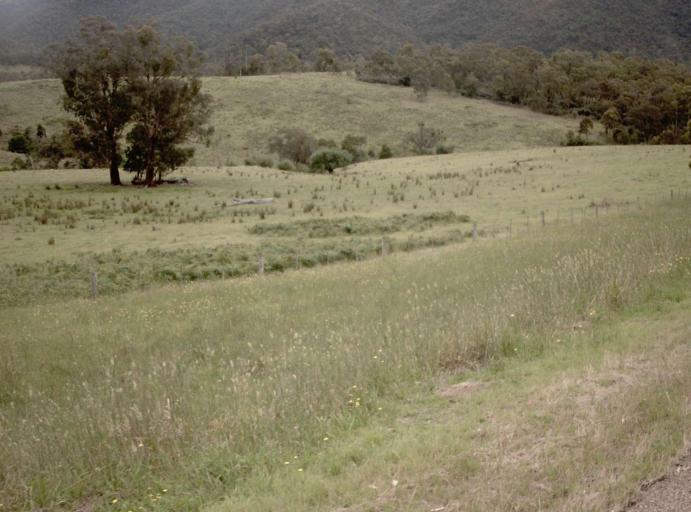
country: AU
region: Victoria
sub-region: East Gippsland
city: Bairnsdale
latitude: -37.5587
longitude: 147.1958
